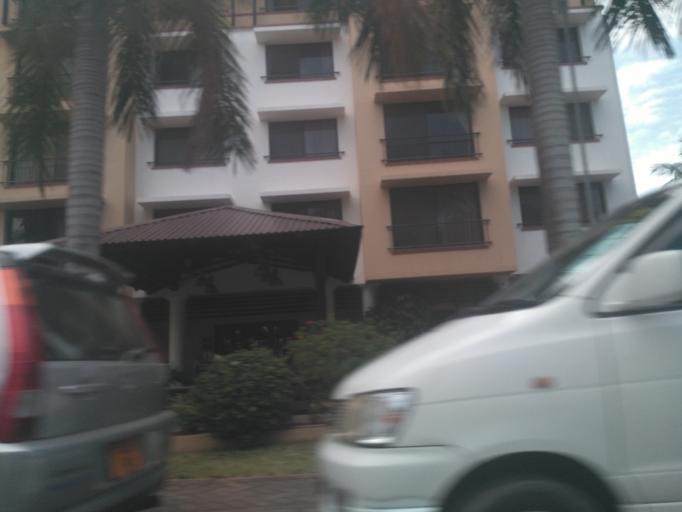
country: TZ
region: Dar es Salaam
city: Magomeni
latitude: -6.7562
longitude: 39.2795
